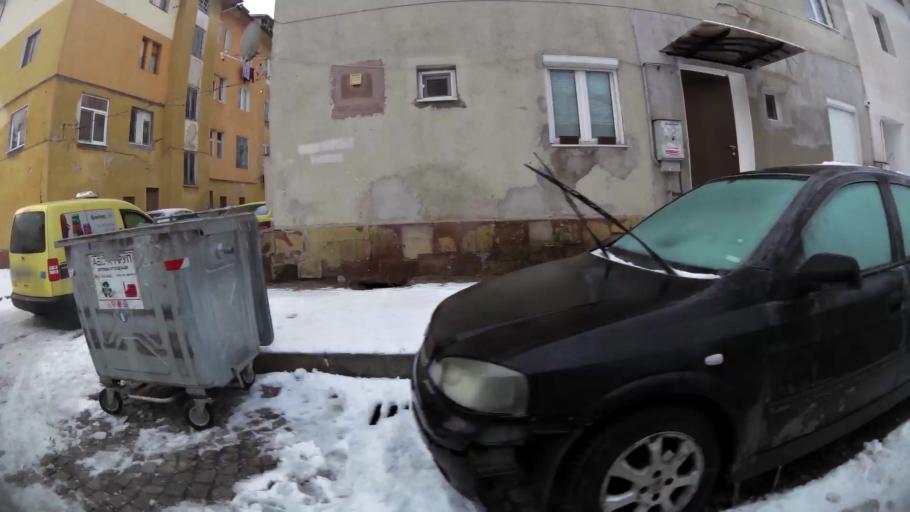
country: BG
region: Sofia-Capital
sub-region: Stolichna Obshtina
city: Sofia
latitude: 42.7154
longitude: 23.2881
